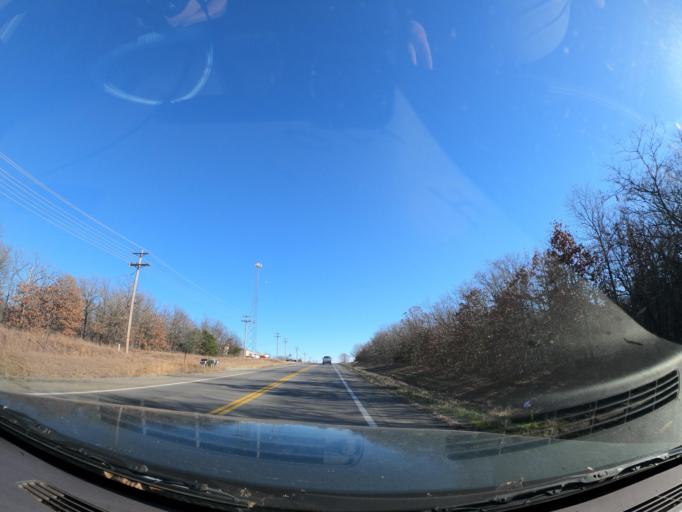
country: US
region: Oklahoma
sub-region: Pittsburg County
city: Longtown
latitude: 35.2369
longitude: -95.4669
